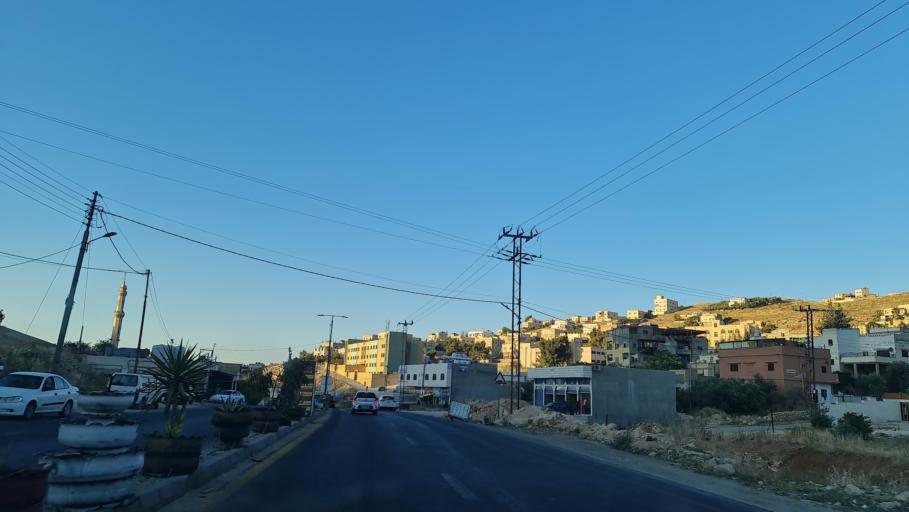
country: JO
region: Amman
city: Al Jubayhah
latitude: 32.0949
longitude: 35.9551
